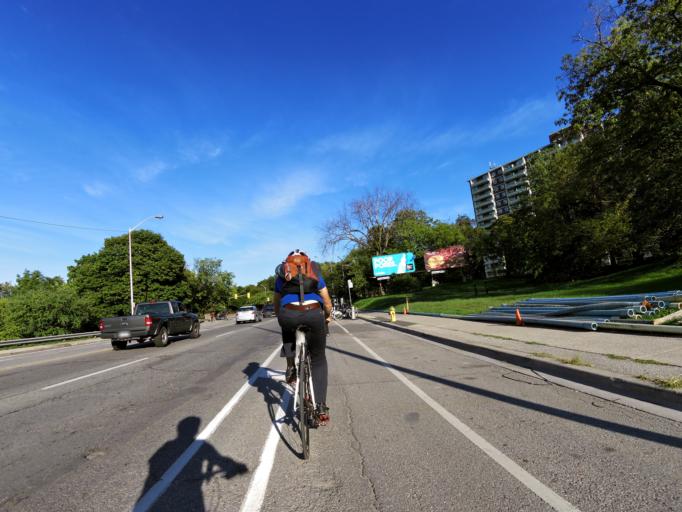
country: CA
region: Ontario
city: Toronto
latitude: 43.6719
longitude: -79.3724
